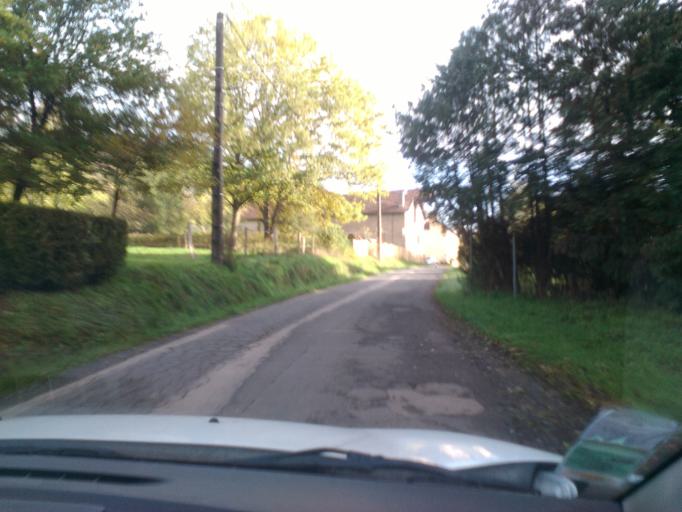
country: FR
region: Lorraine
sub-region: Departement des Vosges
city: Moyenmoutier
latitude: 48.4157
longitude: 6.8747
